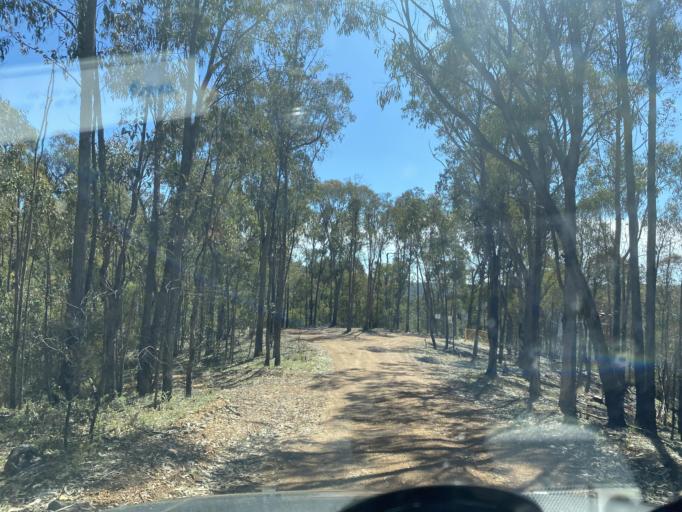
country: AU
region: Victoria
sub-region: Benalla
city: Benalla
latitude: -36.7317
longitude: 146.1829
